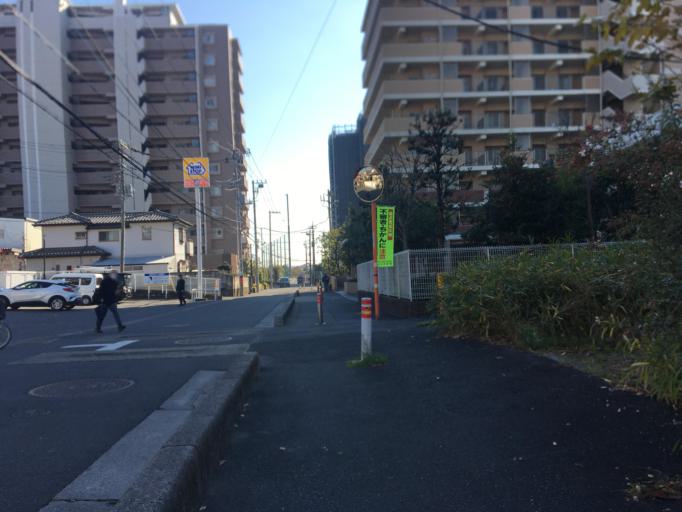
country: JP
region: Saitama
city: Yashio-shi
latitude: 35.8081
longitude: 139.8536
